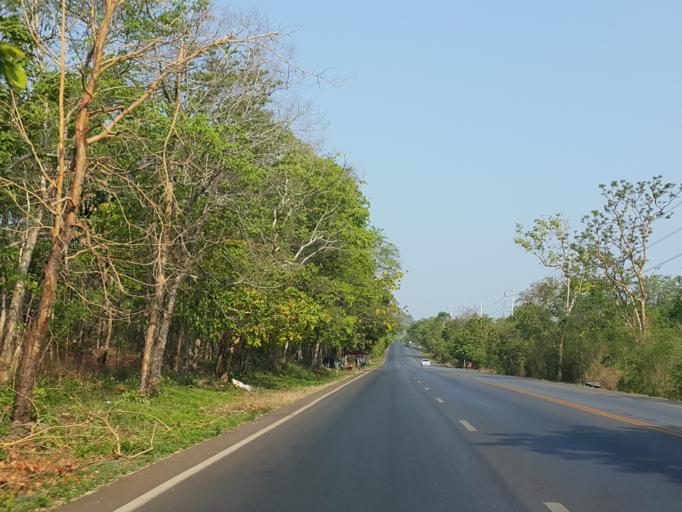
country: TH
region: Kanchanaburi
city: Sai Yok
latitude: 14.1082
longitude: 99.2150
